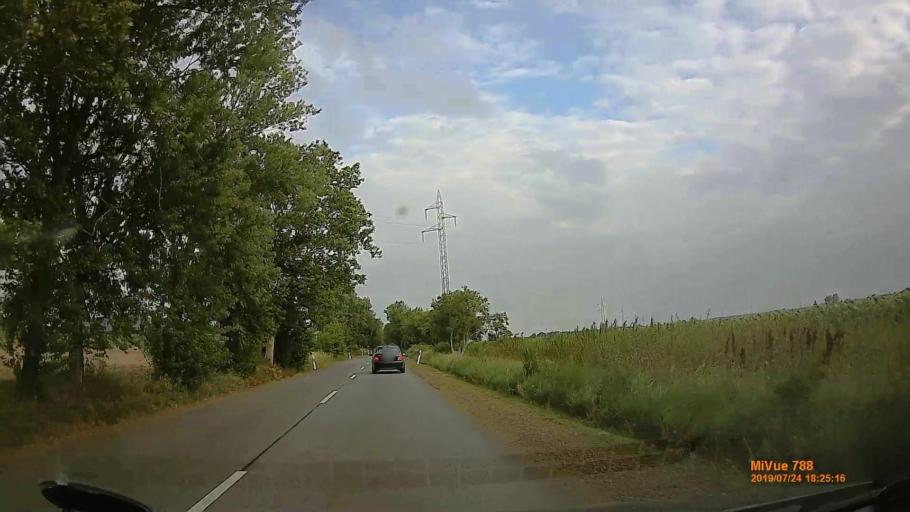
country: HU
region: Borsod-Abauj-Zemplen
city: Tarcal
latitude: 48.1529
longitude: 21.3148
